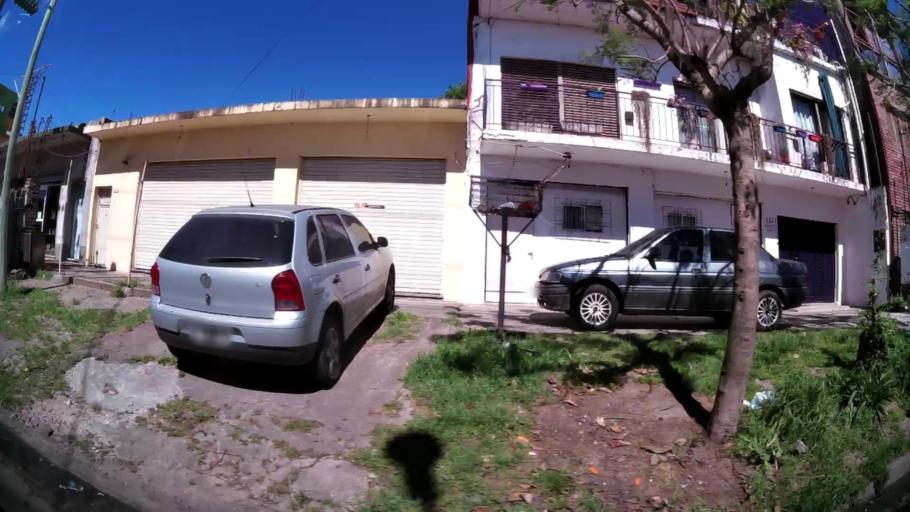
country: AR
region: Buenos Aires
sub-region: Partido de Tigre
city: Tigre
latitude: -34.4953
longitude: -58.6115
